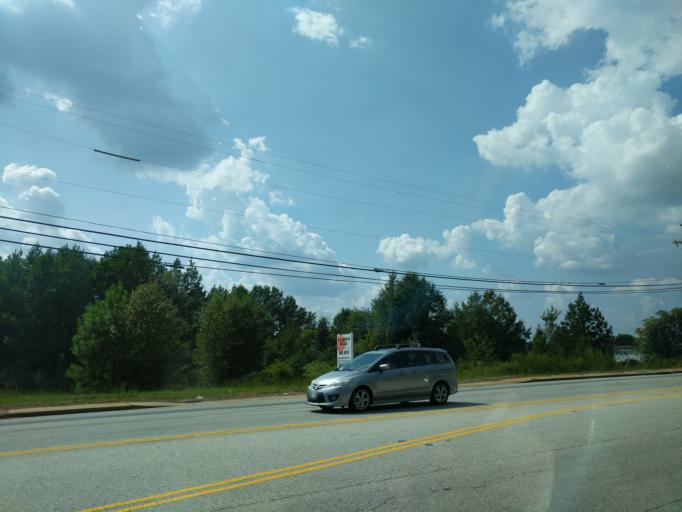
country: US
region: South Carolina
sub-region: Greenville County
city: Five Forks
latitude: 34.8691
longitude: -82.2225
